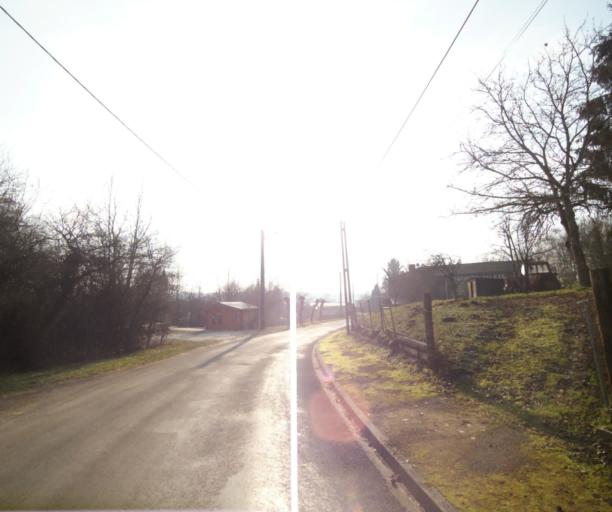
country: FR
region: Champagne-Ardenne
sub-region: Departement de la Haute-Marne
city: Laneuville-a-Remy
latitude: 48.4618
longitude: 4.9150
